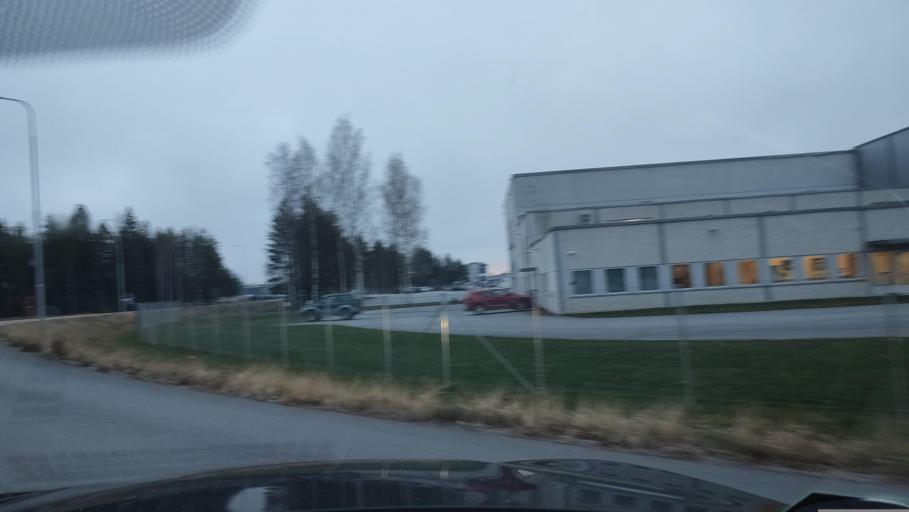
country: FI
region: Southern Ostrobothnia
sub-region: Suupohja
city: Kauhajoki
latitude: 62.4592
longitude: 22.1955
